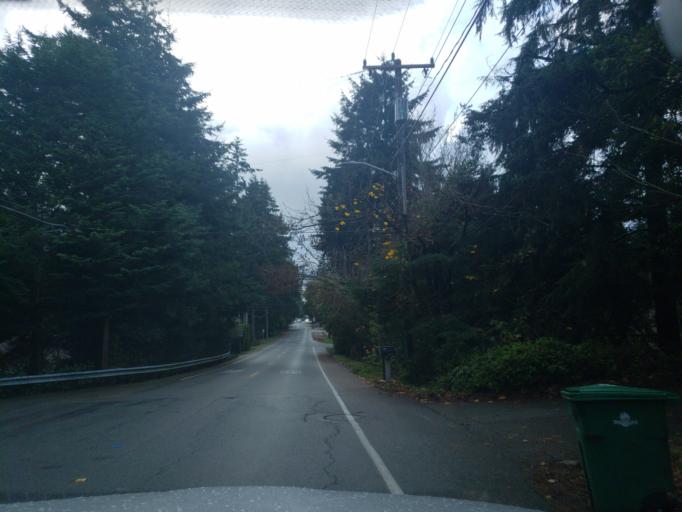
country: US
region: Washington
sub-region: Snohomish County
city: Esperance
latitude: 47.7705
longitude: -122.3569
